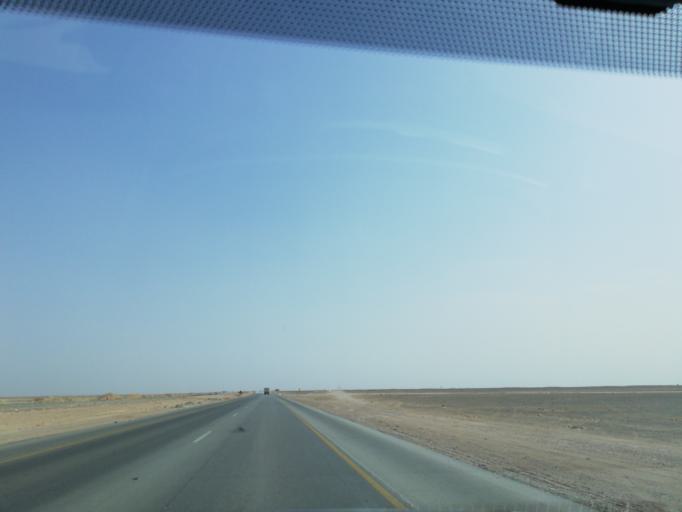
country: OM
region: Muhafazat ad Dakhiliyah
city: Adam
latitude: 21.7090
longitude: 57.3274
